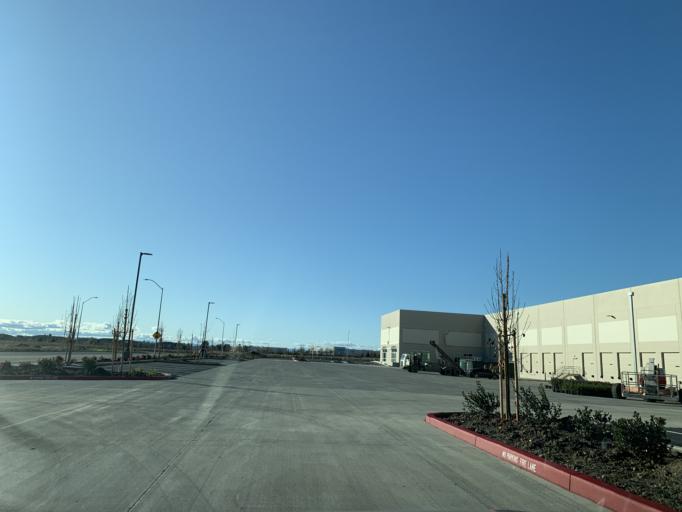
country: US
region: California
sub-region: Yolo County
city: West Sacramento
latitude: 38.5461
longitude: -121.5611
